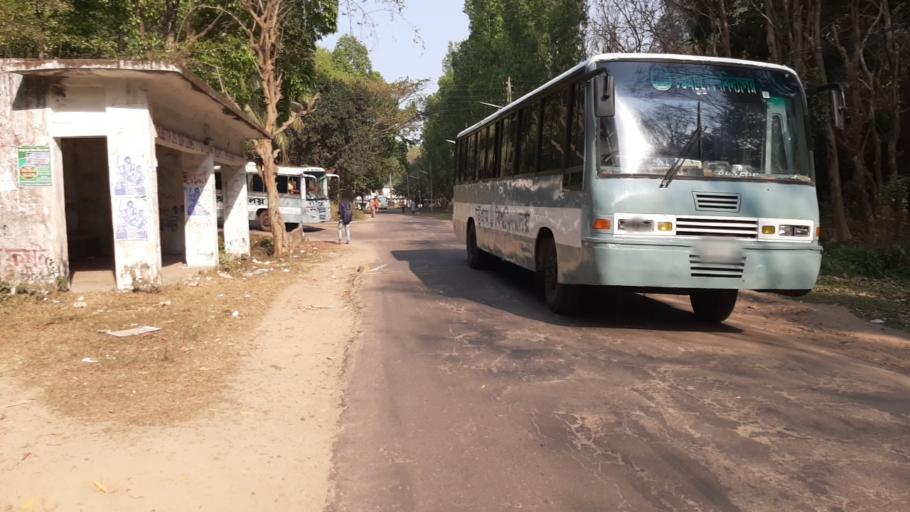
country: BD
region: Chittagong
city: Raojan
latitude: 22.4743
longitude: 91.7913
